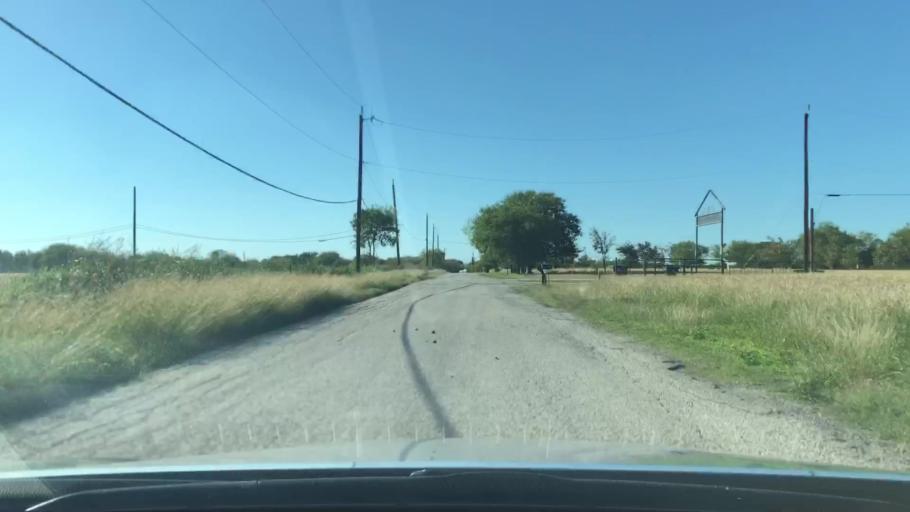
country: US
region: Texas
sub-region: Bexar County
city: Converse
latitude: 29.4671
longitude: -98.2992
